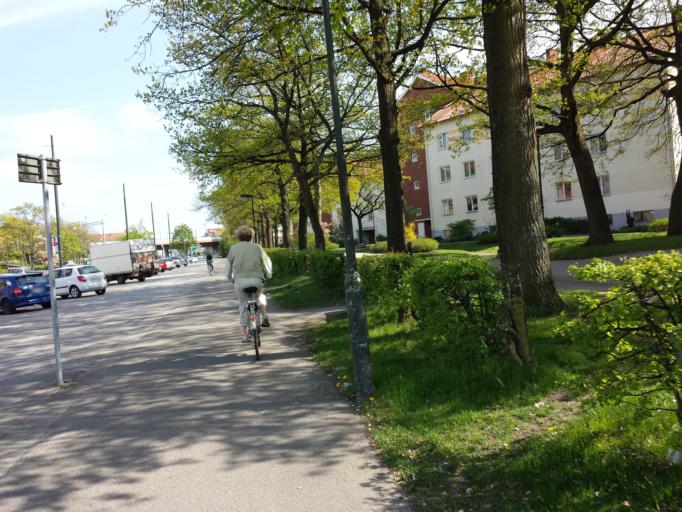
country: SE
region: Skane
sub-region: Malmo
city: Malmoe
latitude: 55.5813
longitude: 13.0261
